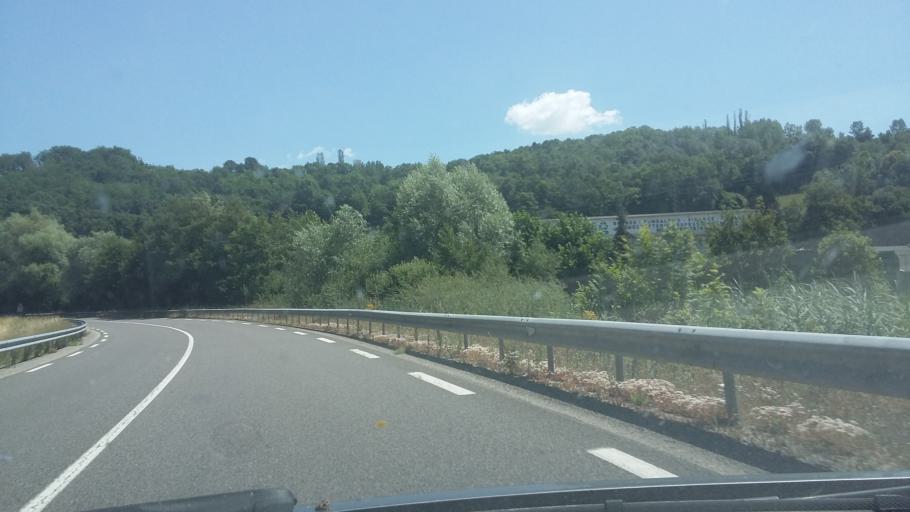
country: FR
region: Rhone-Alpes
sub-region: Departement de l'Ain
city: Belley
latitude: 45.7753
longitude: 5.6934
